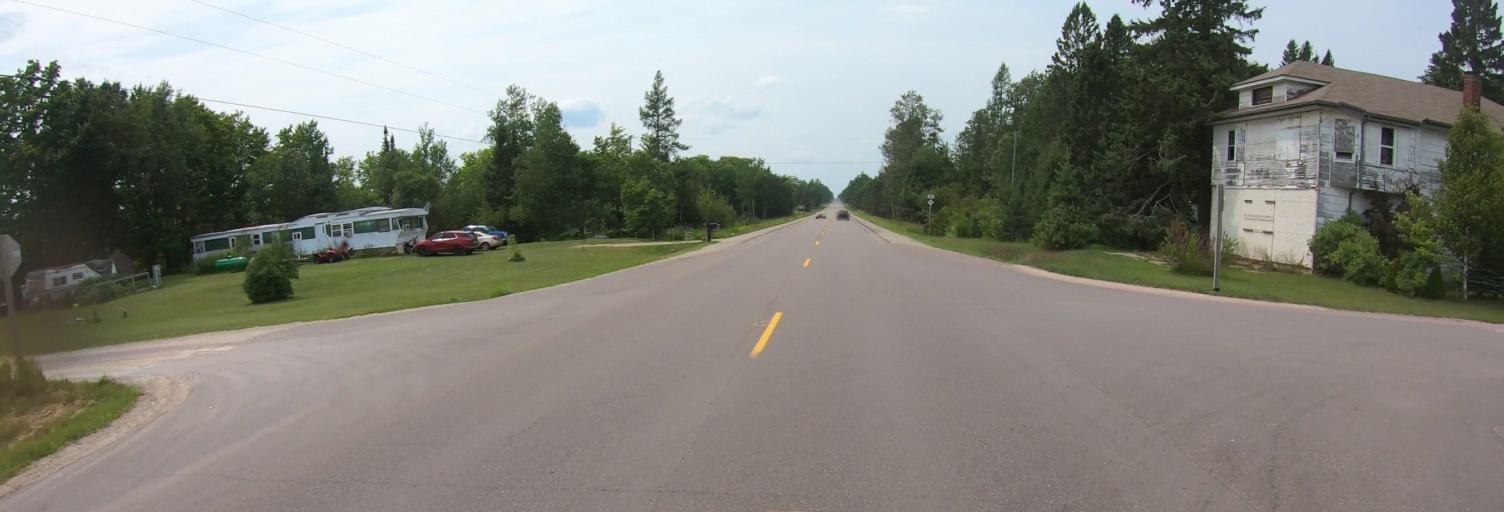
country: US
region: Michigan
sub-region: Marquette County
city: K. I. Sawyer Air Force Base
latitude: 46.3476
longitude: -87.0852
